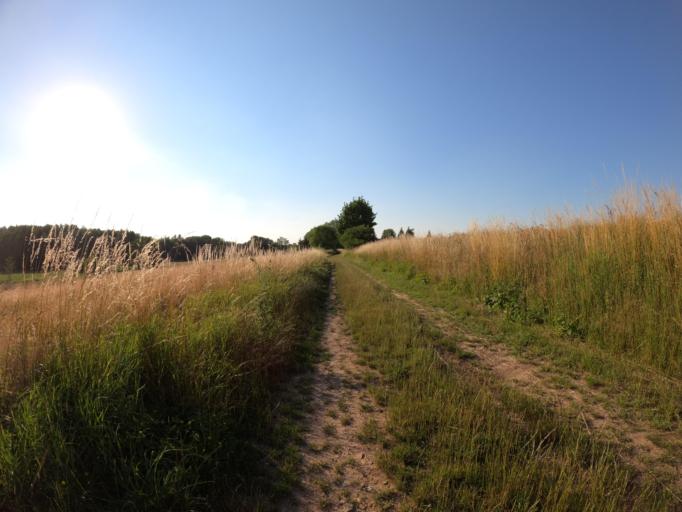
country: DE
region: Brandenburg
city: Tantow
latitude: 53.2494
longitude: 14.3652
